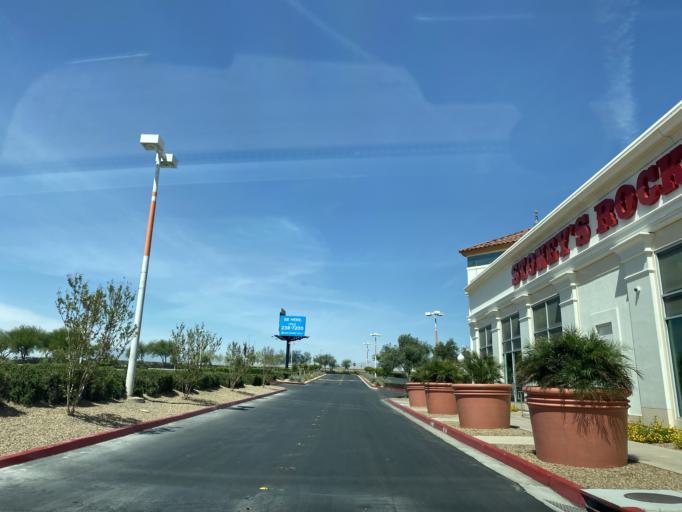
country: US
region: Nevada
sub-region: Clark County
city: Paradise
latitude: 36.0665
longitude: -115.1780
